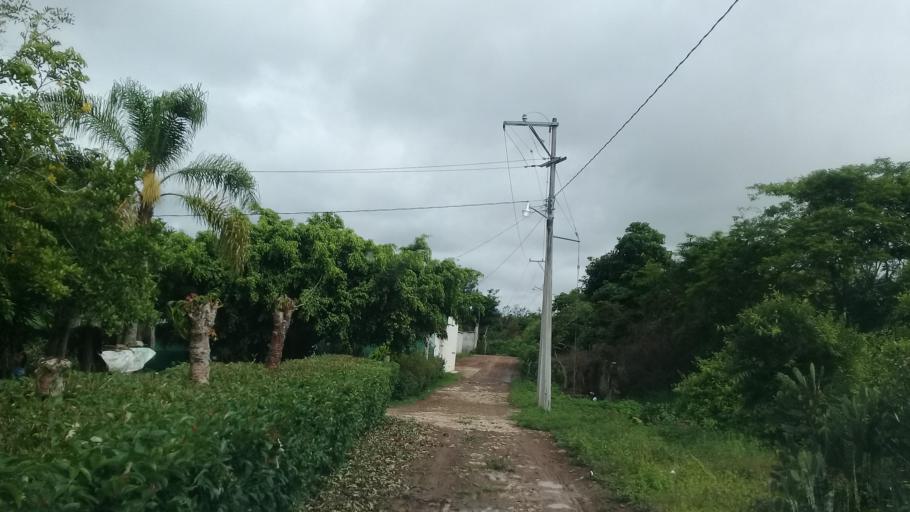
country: MX
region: Veracruz
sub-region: Emiliano Zapata
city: Jacarandas
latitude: 19.4776
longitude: -96.8496
